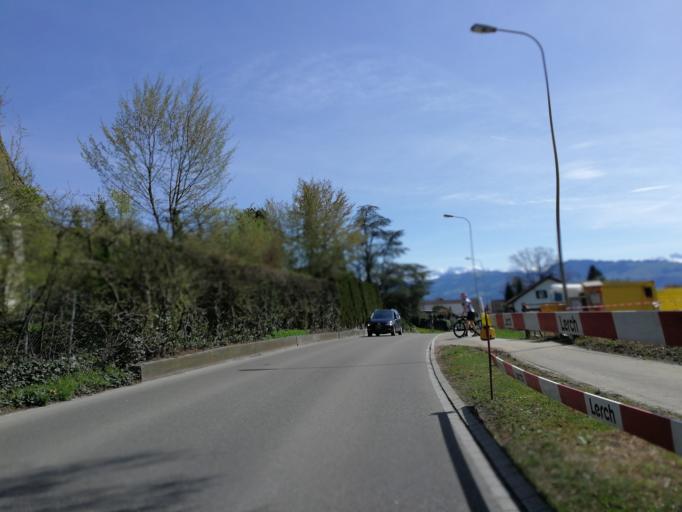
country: CH
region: Zurich
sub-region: Bezirk Meilen
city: Mannedorf
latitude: 47.2560
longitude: 8.7061
